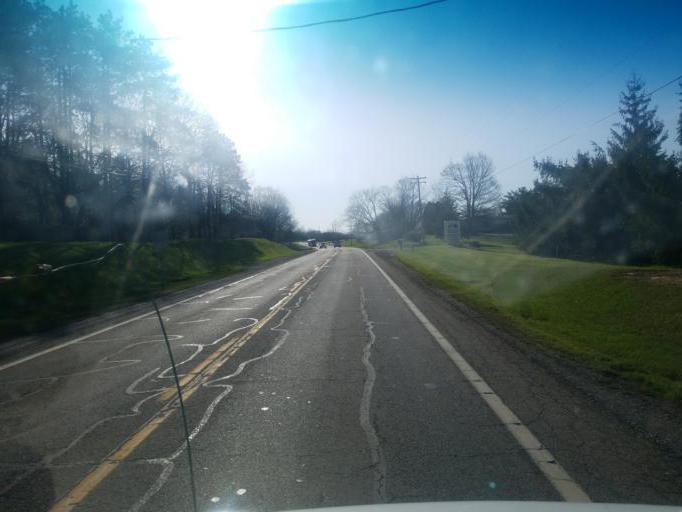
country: US
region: Ohio
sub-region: Morrow County
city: Mount Gilead
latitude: 40.5441
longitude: -82.8109
